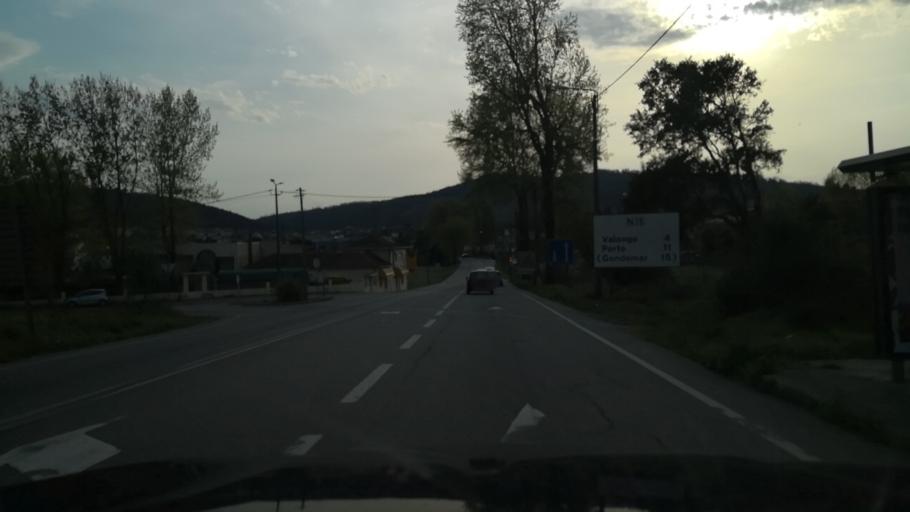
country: PT
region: Porto
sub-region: Valongo
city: Campo
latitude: 41.1841
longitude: -8.4601
